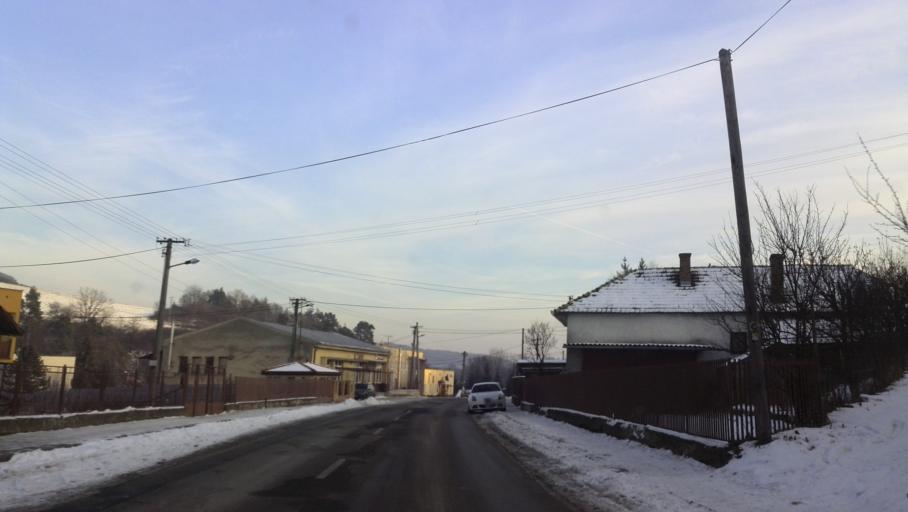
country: SK
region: Presovsky
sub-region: Okres Presov
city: Presov
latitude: 48.9609
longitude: 21.1433
